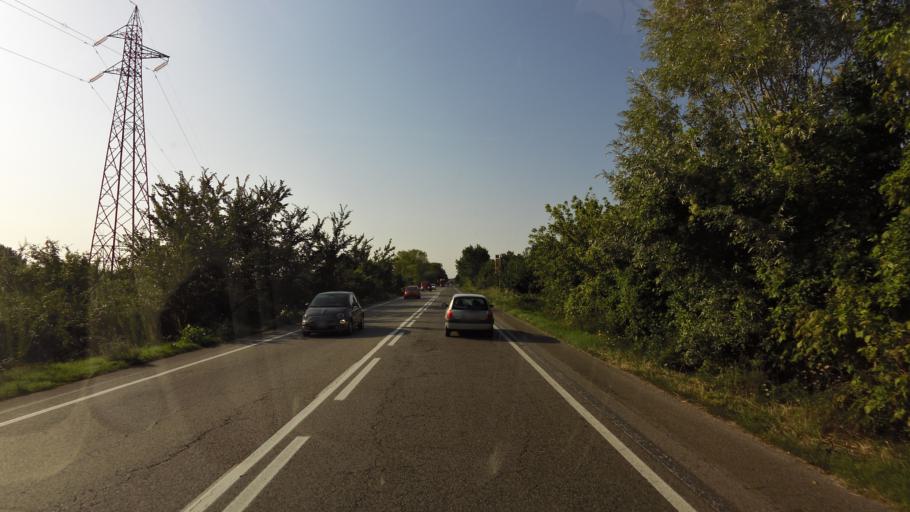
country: IT
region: Emilia-Romagna
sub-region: Provincia di Ravenna
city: Cervia
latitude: 44.2432
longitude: 12.3520
